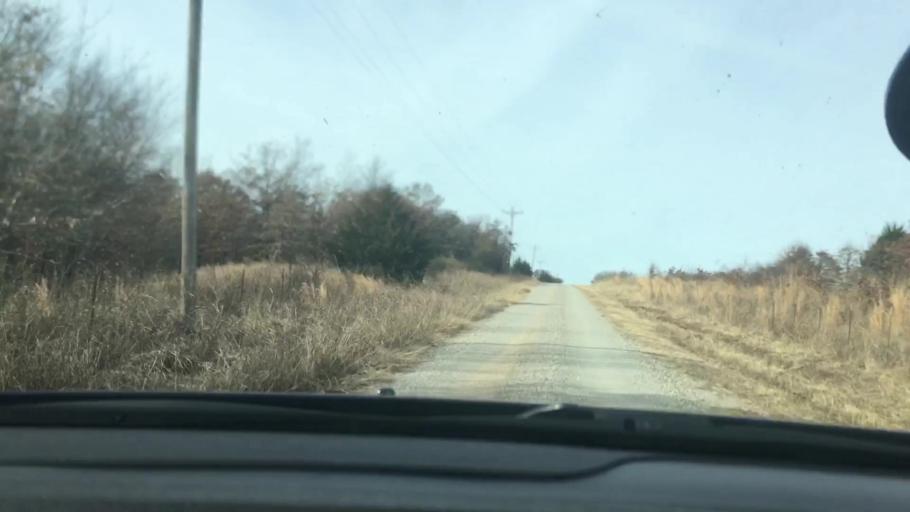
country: US
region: Oklahoma
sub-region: Garvin County
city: Wynnewood
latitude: 34.6374
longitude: -97.2371
